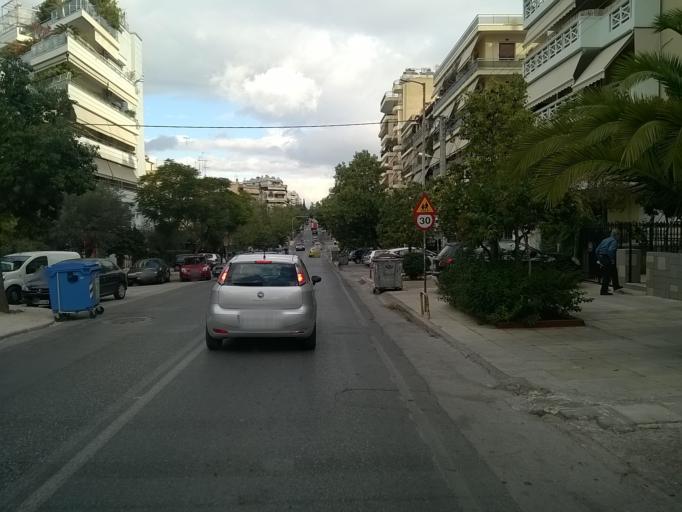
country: GR
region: Attica
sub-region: Nomarchia Athinas
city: Nea Smyrni
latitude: 37.9381
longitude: 23.7162
